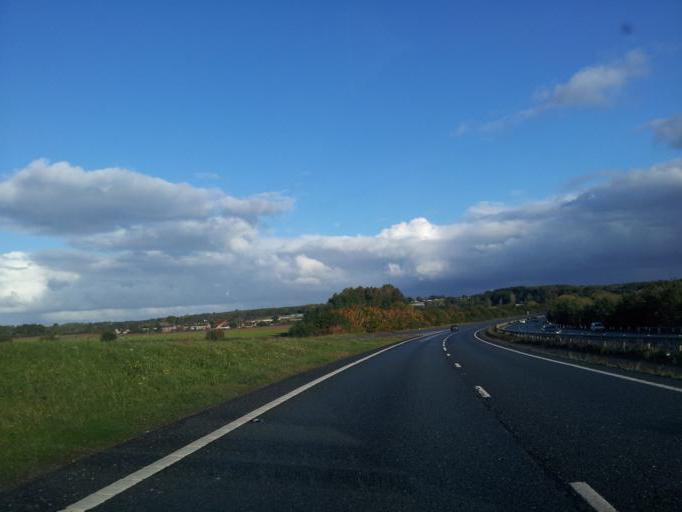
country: GB
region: England
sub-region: Norfolk
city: Bowthorpe
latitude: 52.6271
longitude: 1.1957
